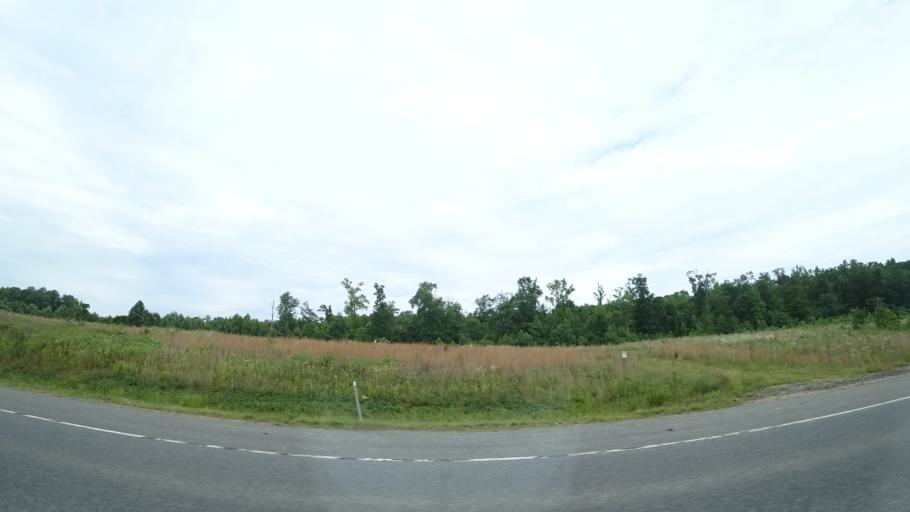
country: US
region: Virginia
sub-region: Spotsylvania County
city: Spotsylvania Courthouse
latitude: 38.1697
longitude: -77.6356
